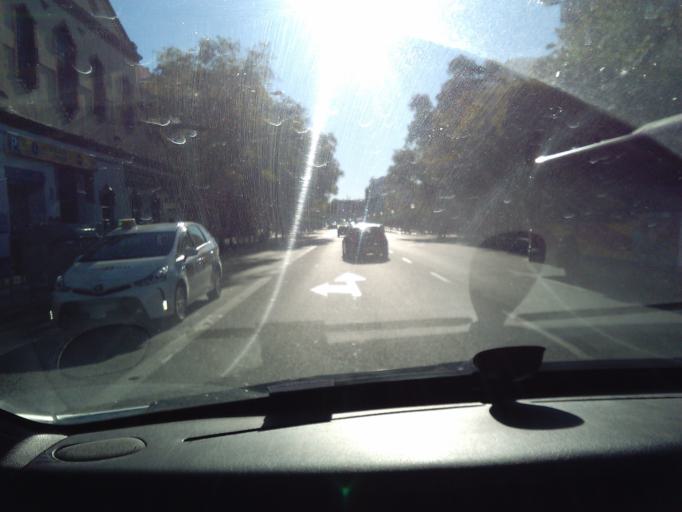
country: ES
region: Andalusia
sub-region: Provincia de Sevilla
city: Sevilla
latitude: 37.3967
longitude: -5.9818
